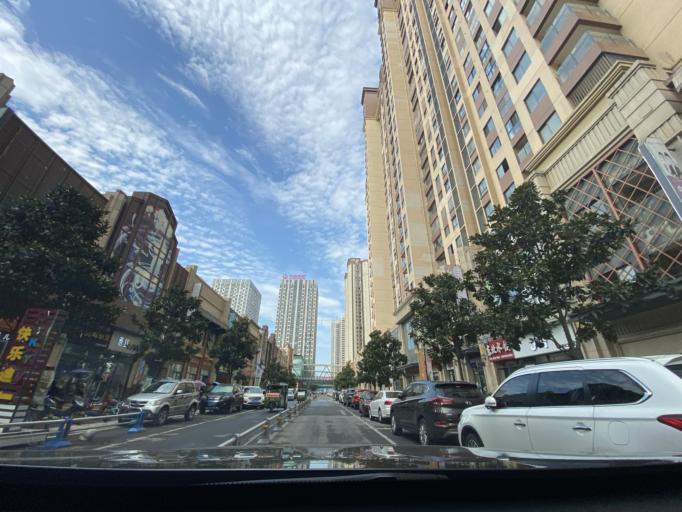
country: CN
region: Sichuan
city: Mianyang
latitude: 31.4131
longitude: 104.7824
